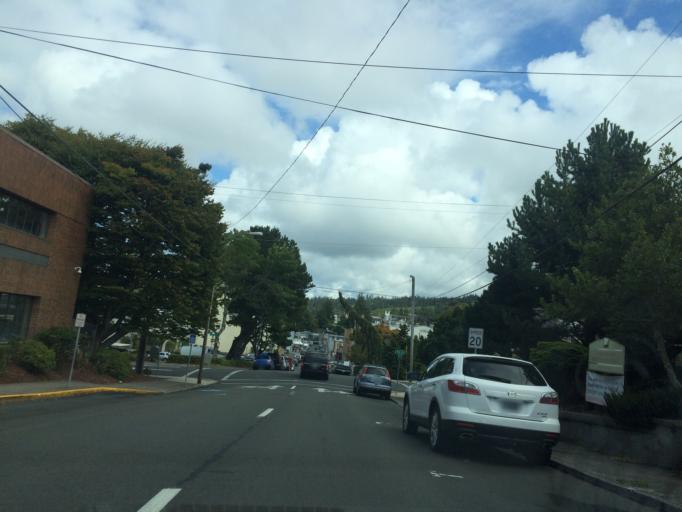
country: US
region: Oregon
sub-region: Clatsop County
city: Astoria
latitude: 46.1877
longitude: -123.8345
